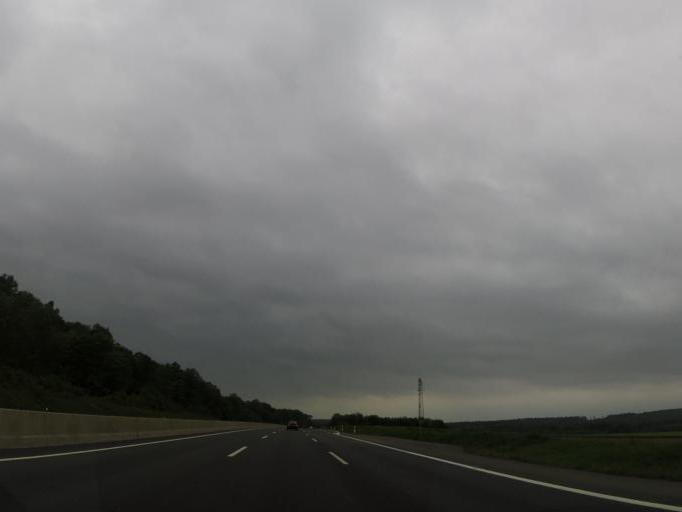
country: DE
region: Lower Saxony
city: Haverlah
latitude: 52.0629
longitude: 10.1933
